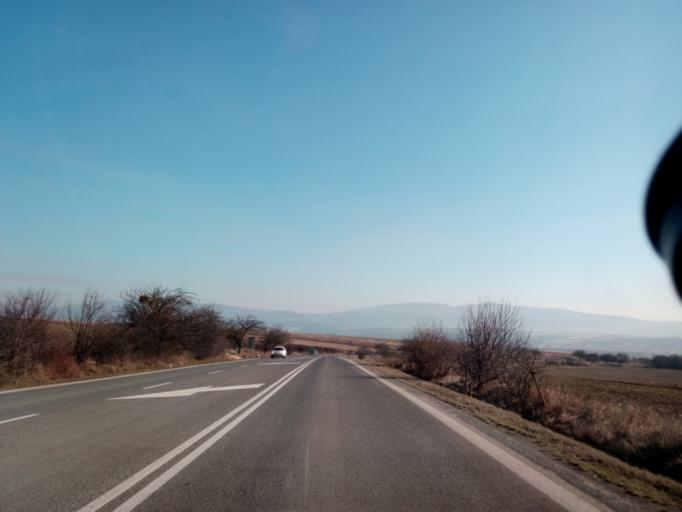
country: SK
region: Kosicky
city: Kosice
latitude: 48.7330
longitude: 21.3889
